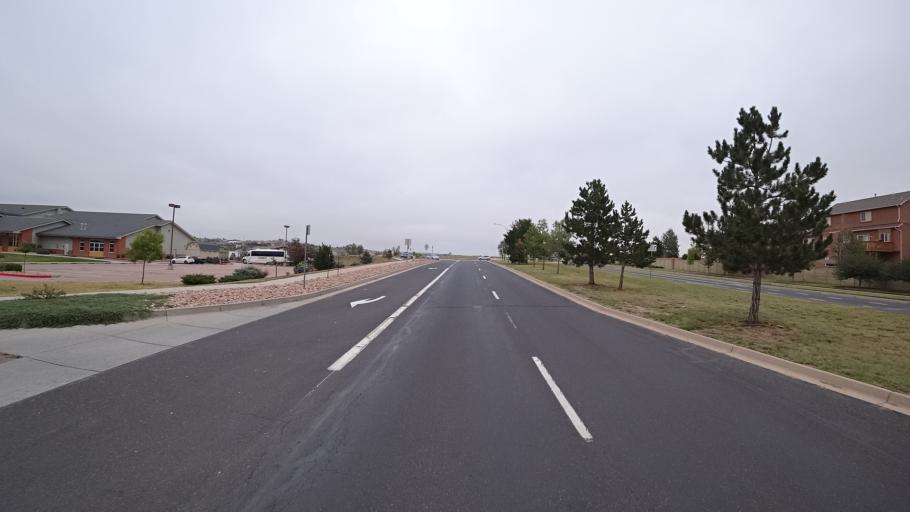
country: US
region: Colorado
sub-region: El Paso County
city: Cimarron Hills
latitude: 38.9252
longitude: -104.6925
